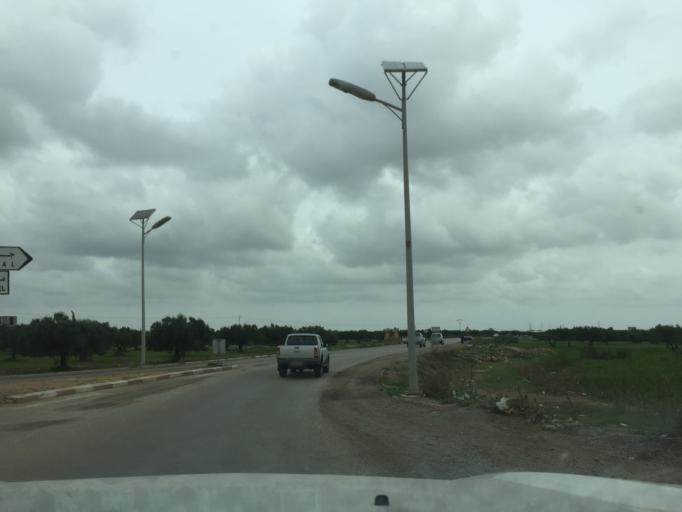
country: TN
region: Al Munastir
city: Manzil Kamil
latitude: 35.6228
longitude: 10.6845
